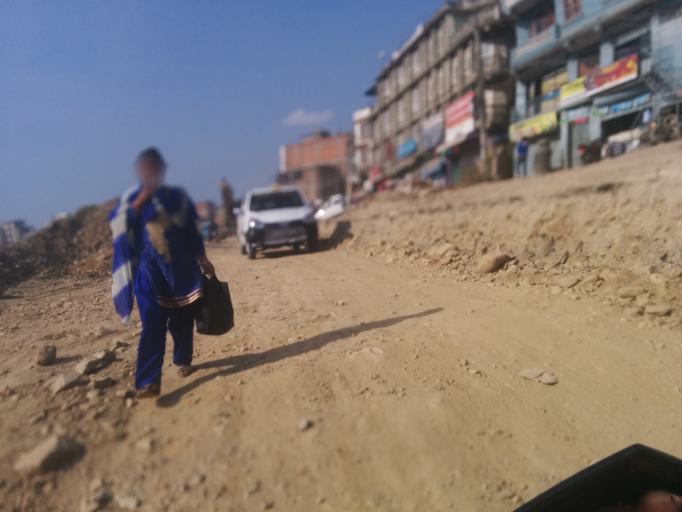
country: NP
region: Central Region
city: Kirtipur
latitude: 27.6919
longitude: 85.2826
